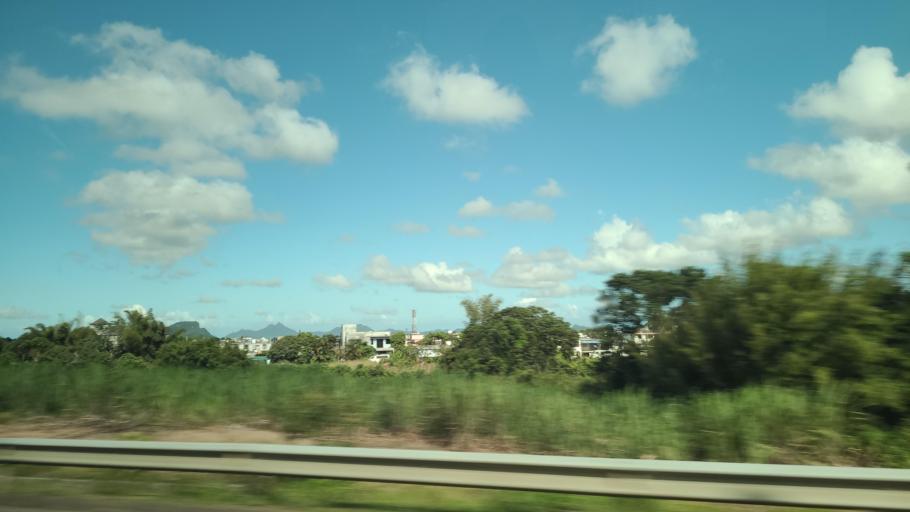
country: MU
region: Moka
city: Quartier Militaire
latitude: -20.2424
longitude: 57.5947
